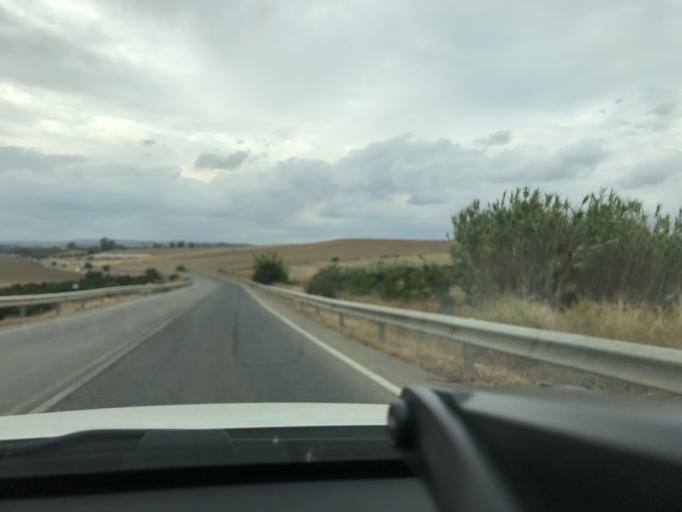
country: ES
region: Andalusia
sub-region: Provincia de Sevilla
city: Villanueva del Rio y Minas
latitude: 37.6350
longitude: -5.7083
